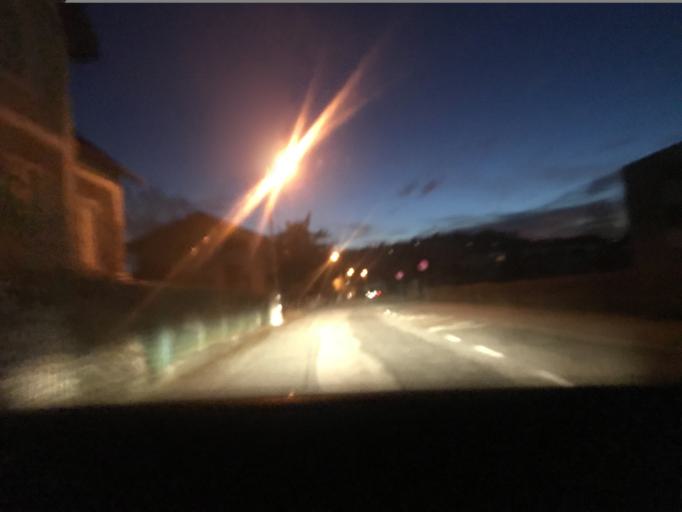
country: AT
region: Styria
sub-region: Politischer Bezirk Leibnitz
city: Leibnitz
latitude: 46.7771
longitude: 15.5422
